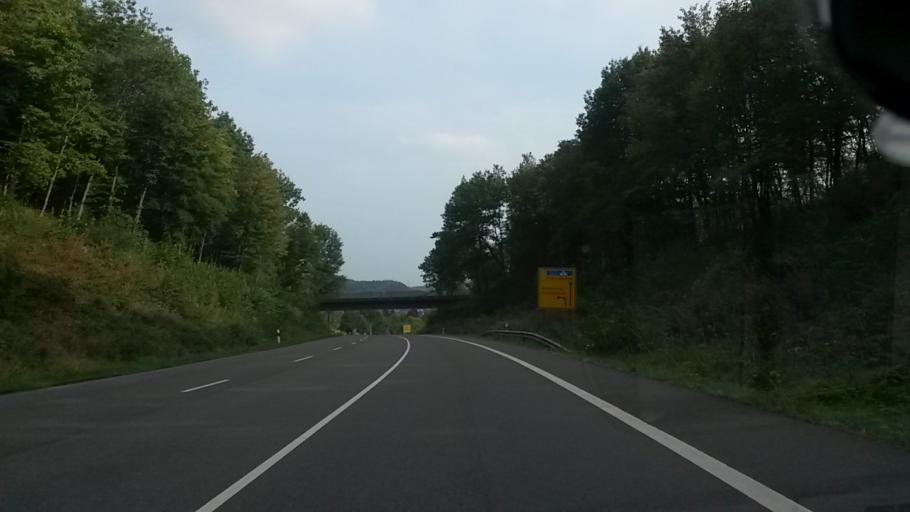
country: DE
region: North Rhine-Westphalia
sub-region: Regierungsbezirk Koln
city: Engelskirchen
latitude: 50.9937
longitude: 7.4282
